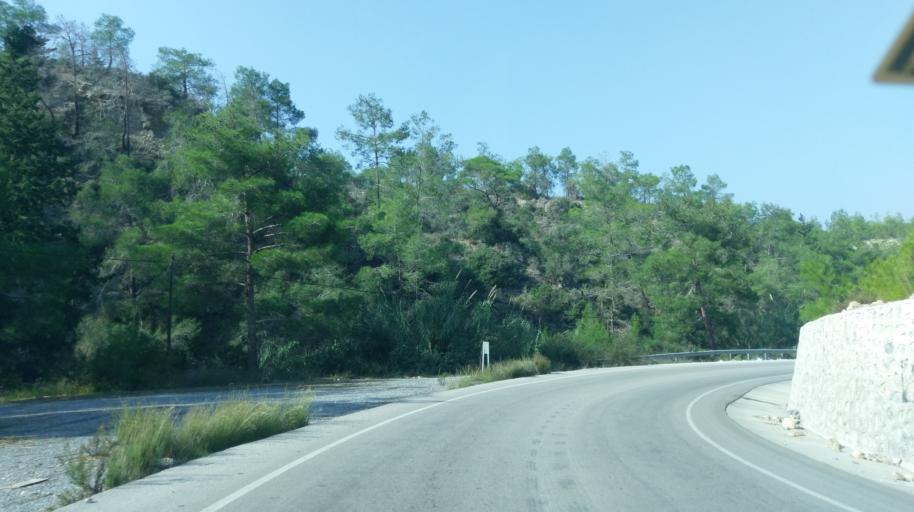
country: CY
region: Ammochostos
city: Lefkonoiko
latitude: 35.3558
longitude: 33.7131
